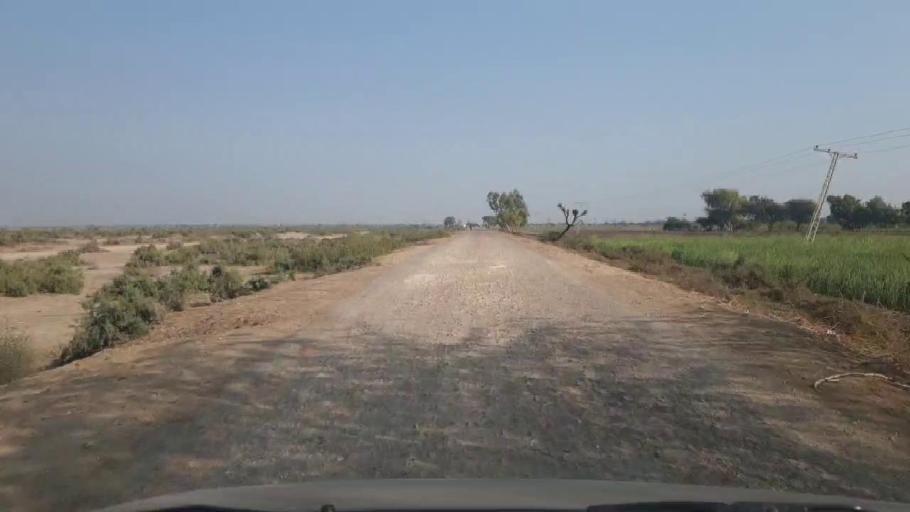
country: PK
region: Sindh
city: Digri
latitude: 25.2385
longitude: 69.1936
